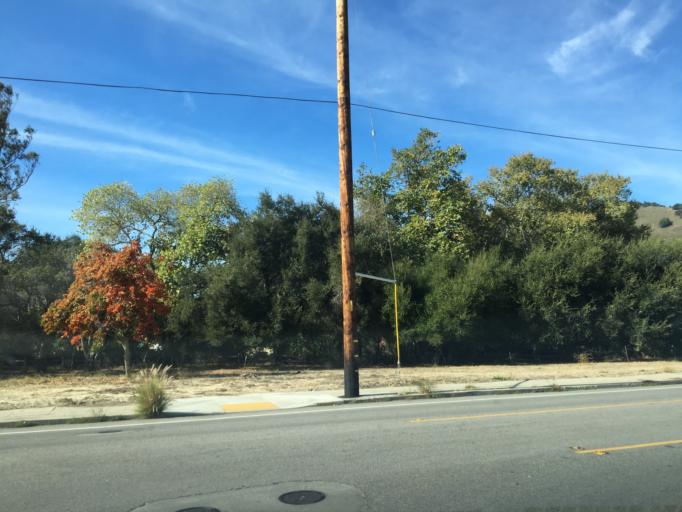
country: US
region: California
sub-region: San Luis Obispo County
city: San Luis Obispo
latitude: 35.2737
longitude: -120.6695
